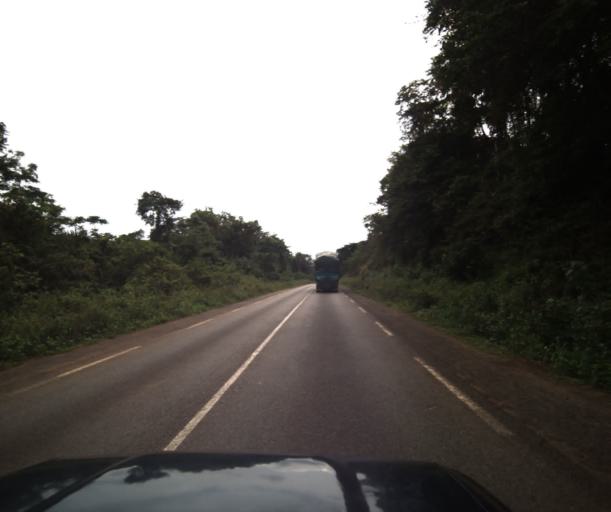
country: CM
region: Littoral
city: Edea
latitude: 3.8191
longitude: 10.3745
